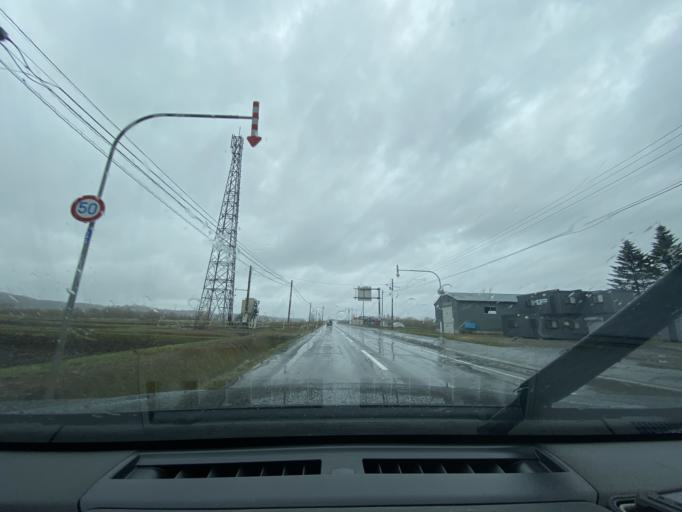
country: JP
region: Hokkaido
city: Fukagawa
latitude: 43.8090
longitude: 142.0197
